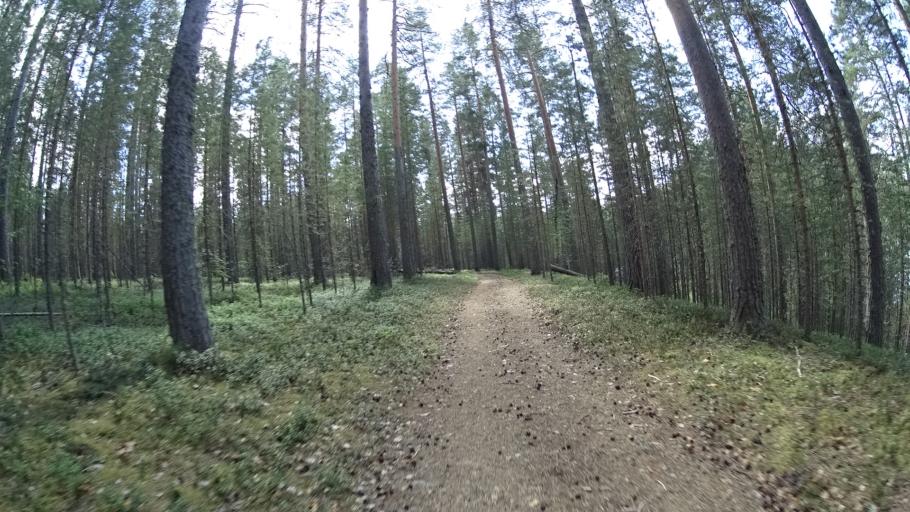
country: FI
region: Southern Savonia
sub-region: Savonlinna
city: Punkaharju
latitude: 61.7887
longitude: 29.3076
